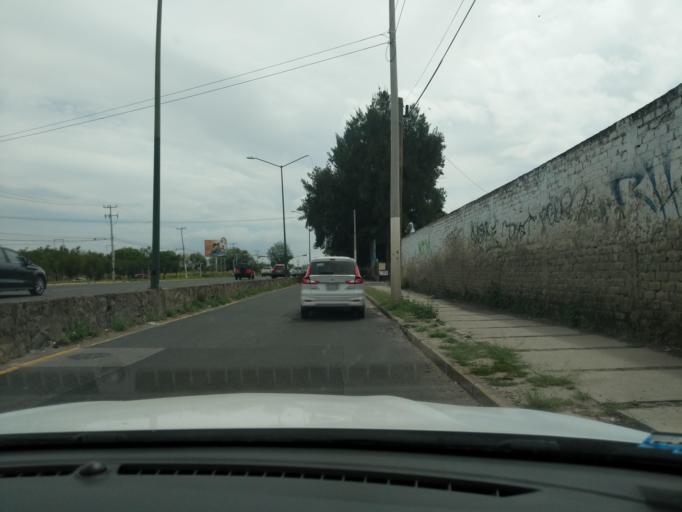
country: MX
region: Jalisco
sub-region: Zapopan
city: Puerta del Llano
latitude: 20.7852
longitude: -103.4684
